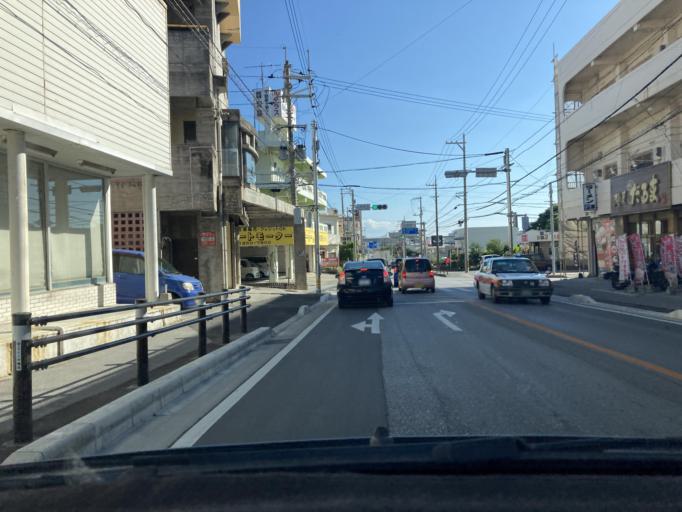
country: JP
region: Okinawa
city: Tomigusuku
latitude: 26.1795
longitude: 127.6647
